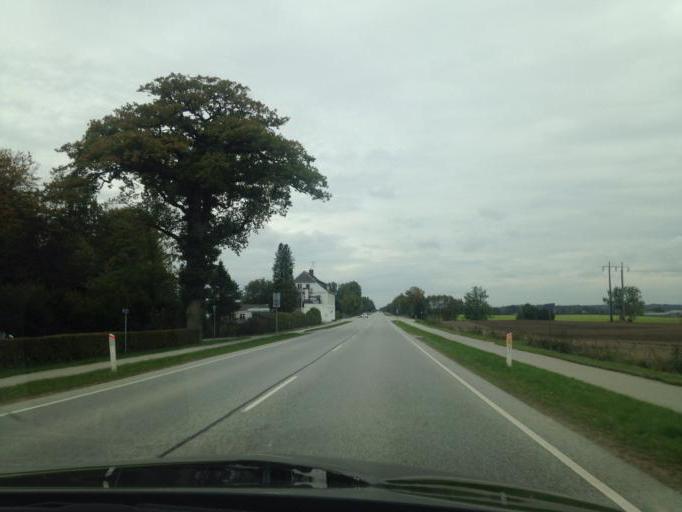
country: DK
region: South Denmark
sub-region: Haderslev Kommune
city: Haderslev
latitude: 55.2829
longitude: 9.4983
